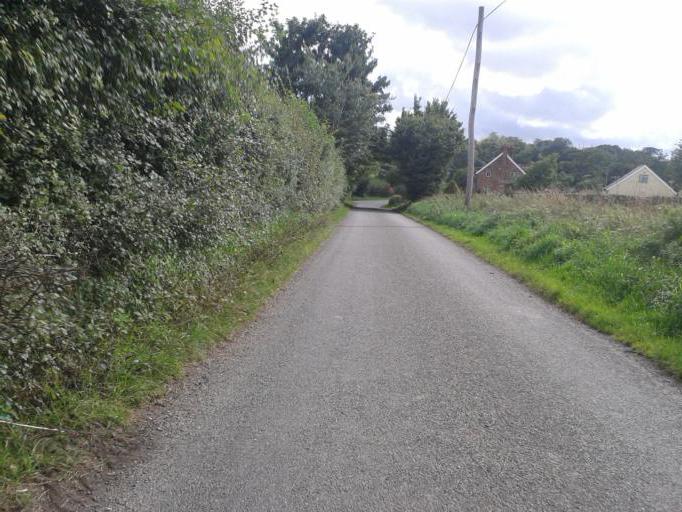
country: GB
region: England
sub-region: Hertfordshire
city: Buntingford
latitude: 51.9771
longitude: 0.0918
